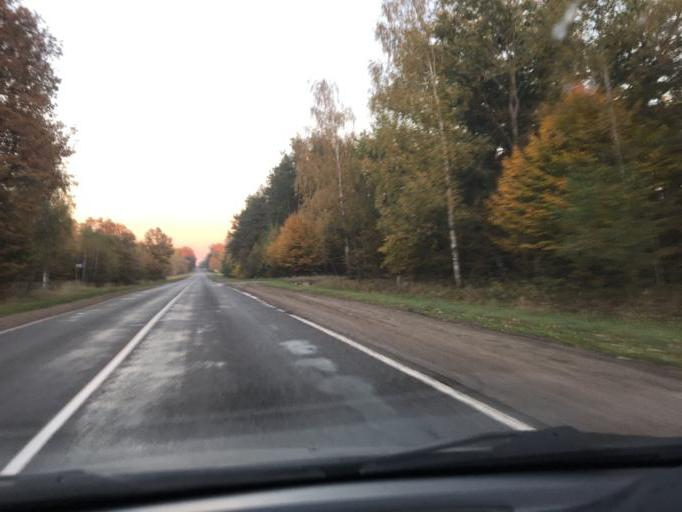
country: BY
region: Mogilev
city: Hlusha
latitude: 53.0962
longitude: 28.9869
